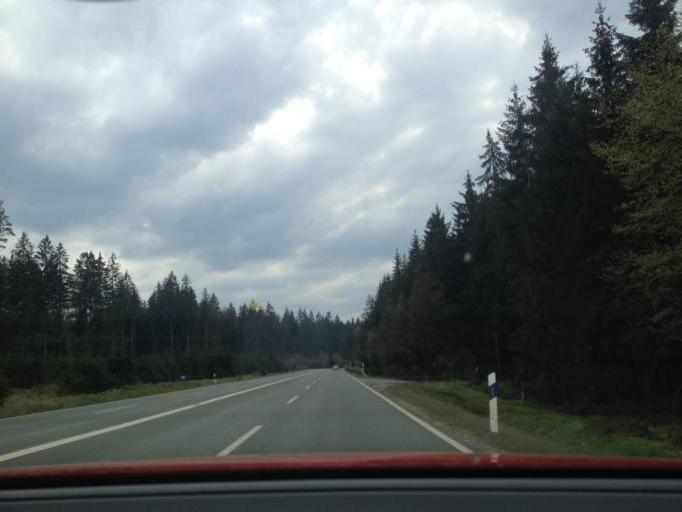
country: DE
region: Bavaria
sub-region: Upper Franconia
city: Nagel
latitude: 50.0048
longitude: 11.9214
